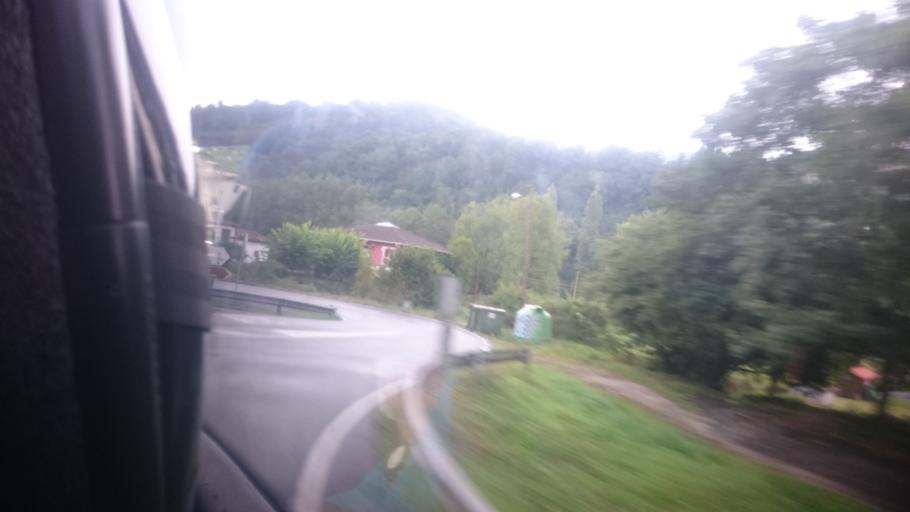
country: ES
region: Asturias
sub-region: Province of Asturias
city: Cangas de Onis
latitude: 43.3507
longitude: -5.0952
